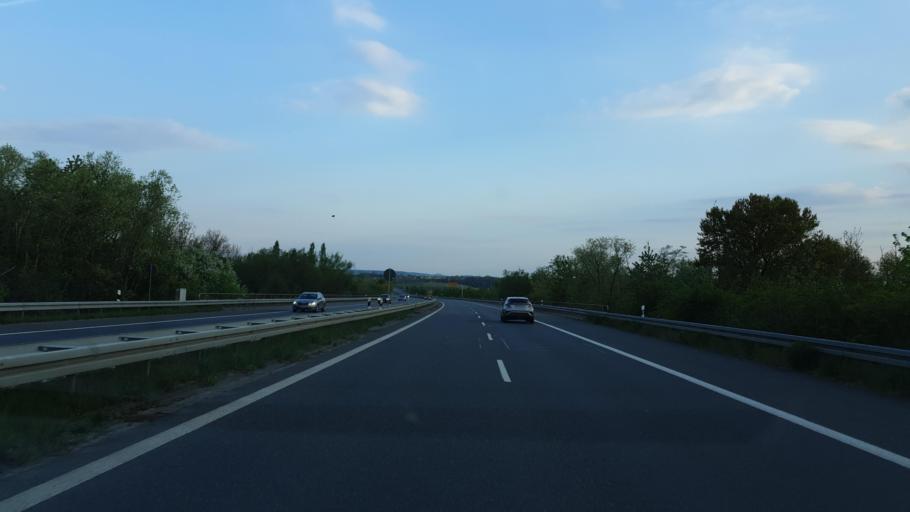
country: DE
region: Saxony
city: Pirna
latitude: 50.9731
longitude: 13.9155
